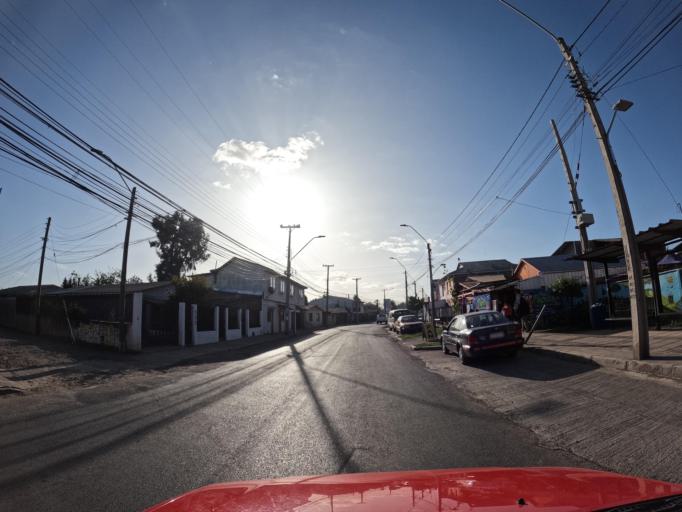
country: CL
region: O'Higgins
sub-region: Provincia de Colchagua
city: Santa Cruz
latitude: -34.6475
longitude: -71.3610
